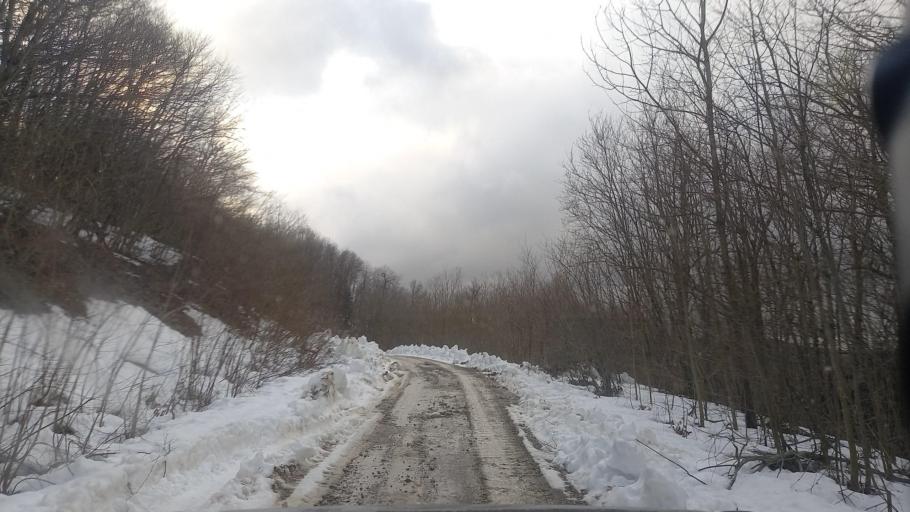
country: RU
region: Krasnodarskiy
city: Dzhubga
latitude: 44.5102
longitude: 38.7717
